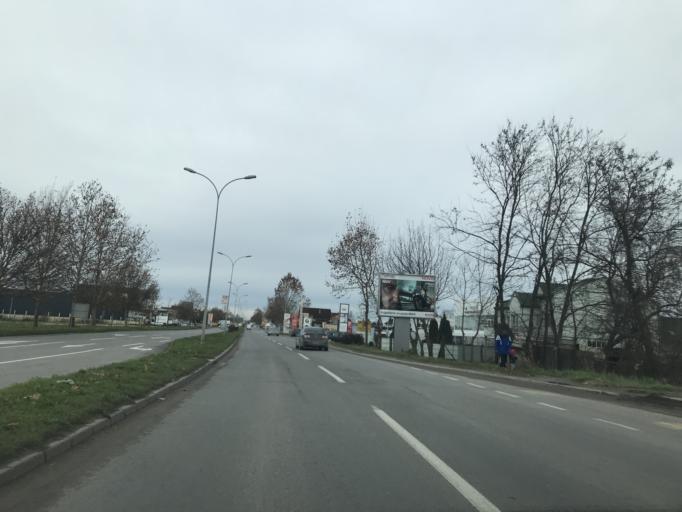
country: RS
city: Veternik
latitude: 45.2452
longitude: 19.7747
